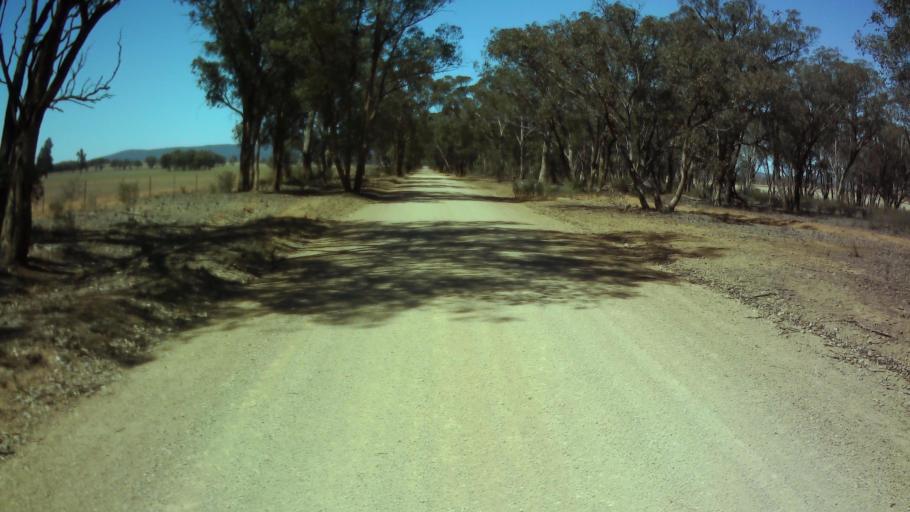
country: AU
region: New South Wales
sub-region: Weddin
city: Grenfell
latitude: -33.8936
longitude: 148.0855
